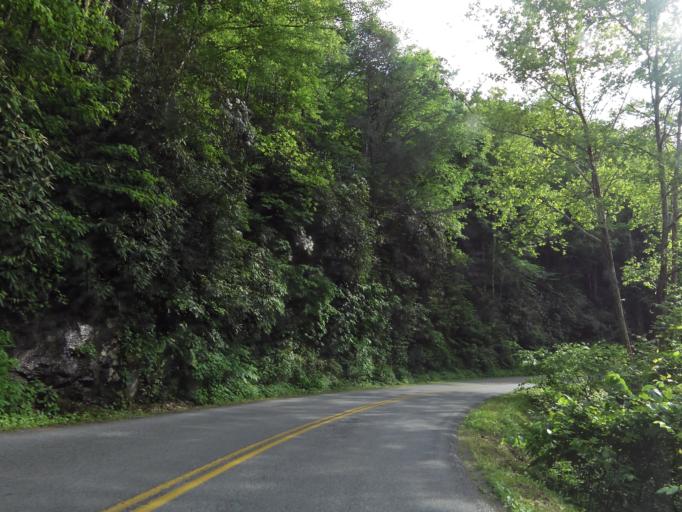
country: US
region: Tennessee
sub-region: Sevier County
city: Gatlinburg
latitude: 35.6794
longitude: -83.6534
